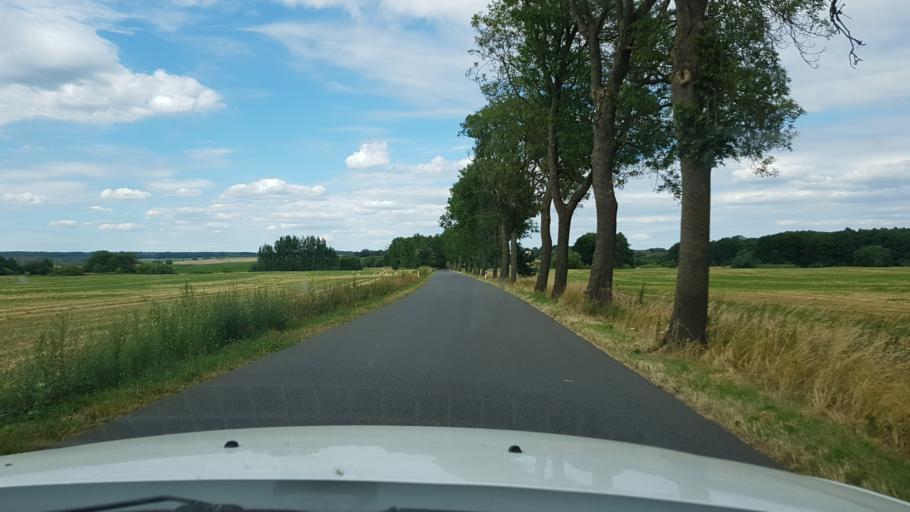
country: PL
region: West Pomeranian Voivodeship
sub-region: Powiat drawski
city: Kalisz Pomorski
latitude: 53.3247
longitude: 15.9249
